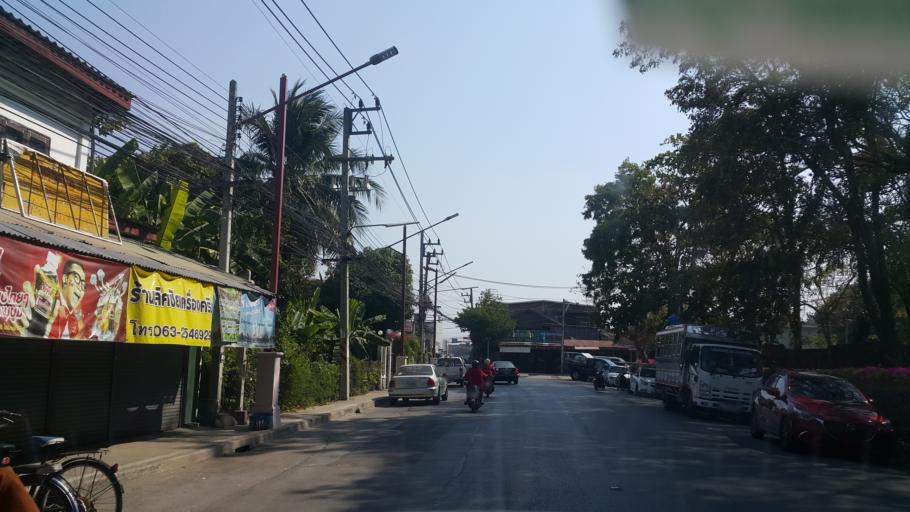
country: TH
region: Nakhon Ratchasima
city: Phimai
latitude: 15.2207
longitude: 102.4952
